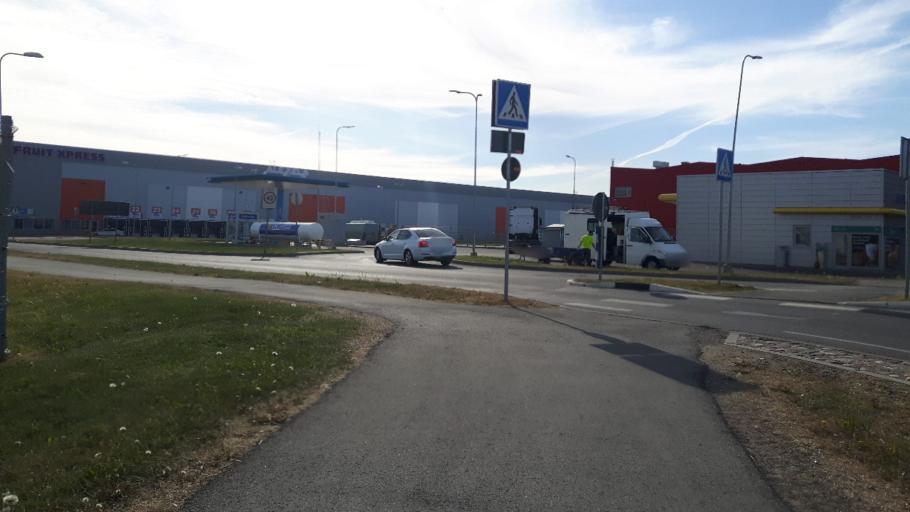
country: EE
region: Harju
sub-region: Joelaehtme vald
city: Loo
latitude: 59.4429
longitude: 24.9303
